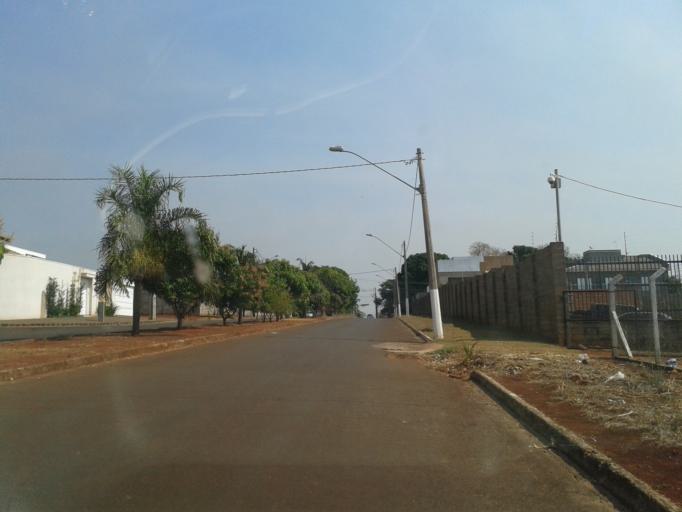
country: BR
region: Minas Gerais
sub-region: Ituiutaba
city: Ituiutaba
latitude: -18.9665
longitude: -49.4440
